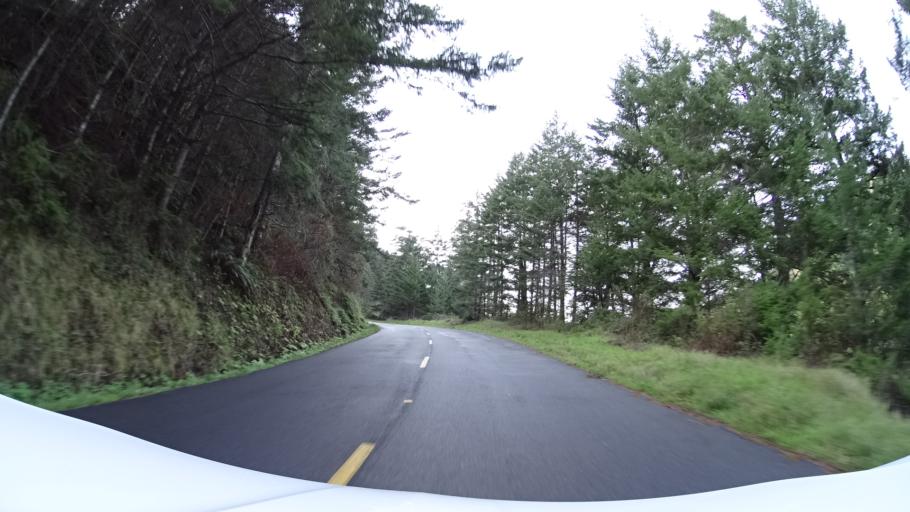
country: US
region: California
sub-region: Humboldt County
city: Ferndale
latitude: 40.3456
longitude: -124.3444
